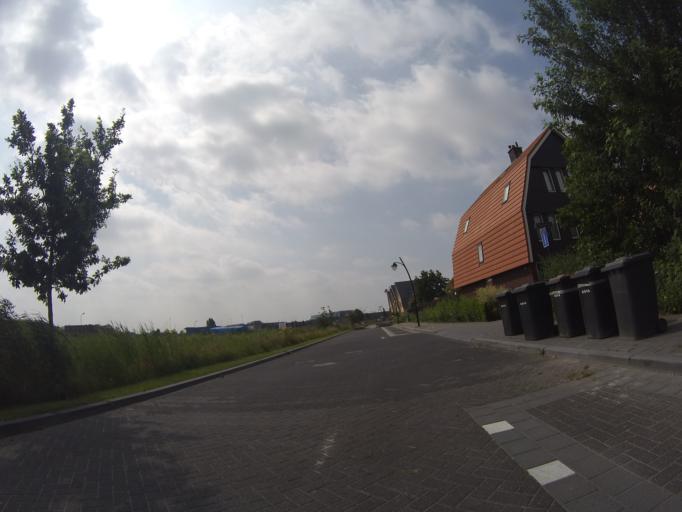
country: NL
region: Utrecht
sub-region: Gemeente Amersfoort
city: Hoogland
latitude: 52.1911
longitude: 5.4143
